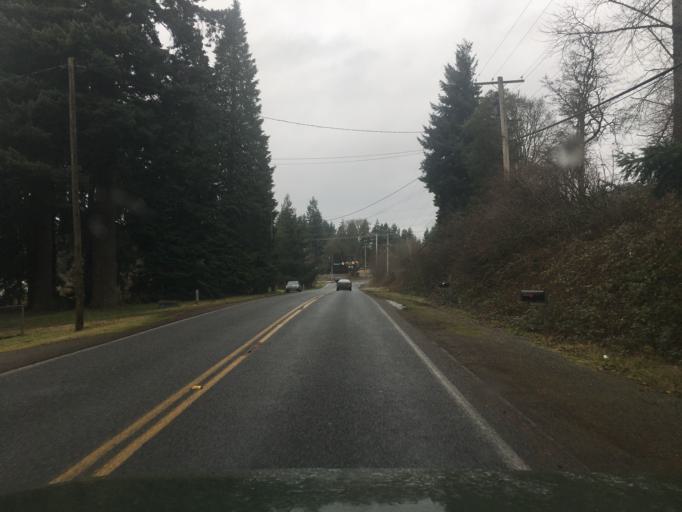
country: US
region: Washington
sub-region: Thurston County
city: Tanglewilde-Thompson Place
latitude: 47.0408
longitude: -122.7815
